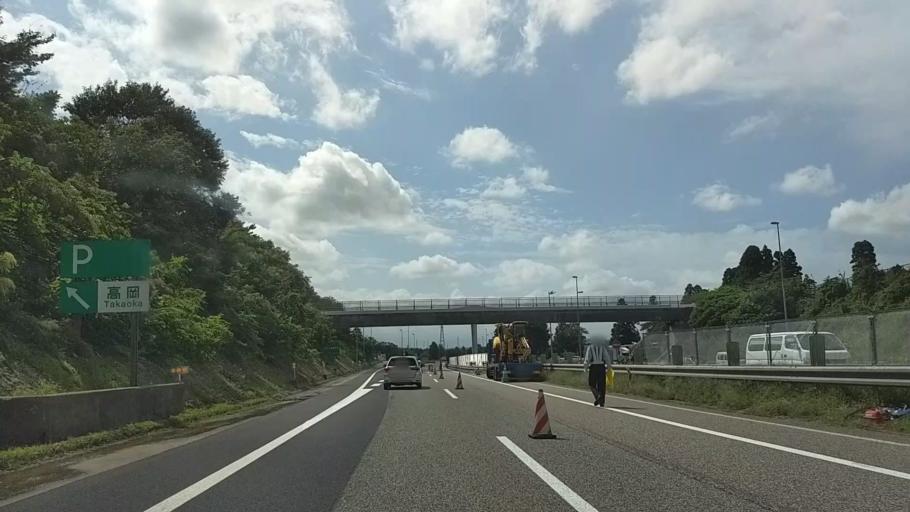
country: JP
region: Toyama
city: Takaoka
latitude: 36.6722
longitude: 137.0327
